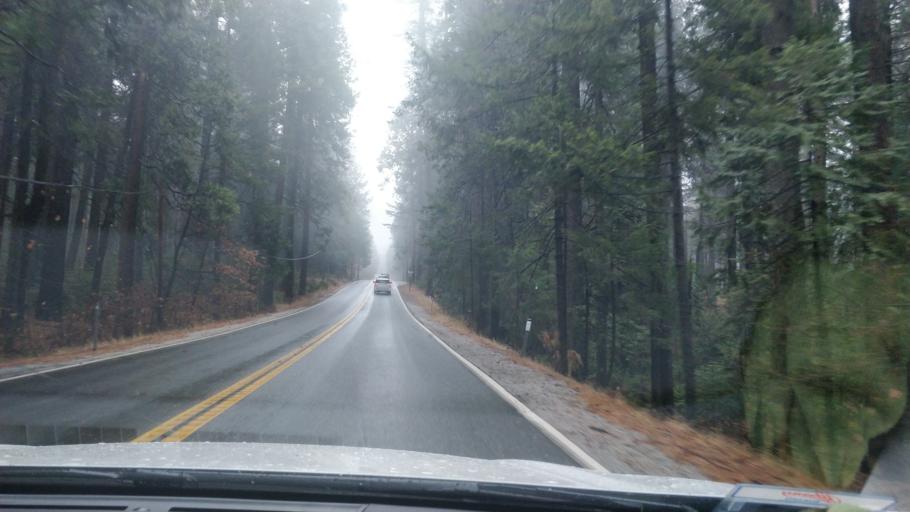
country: US
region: California
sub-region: Nevada County
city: Nevada City
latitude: 39.3228
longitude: -120.8683
